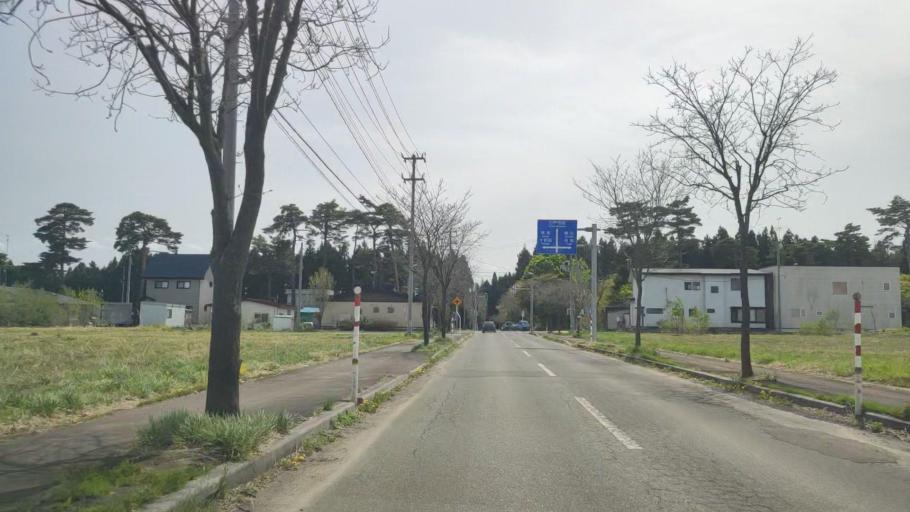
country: JP
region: Aomori
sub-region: Misawa Shi
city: Inuotose
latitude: 40.7169
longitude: 141.1504
